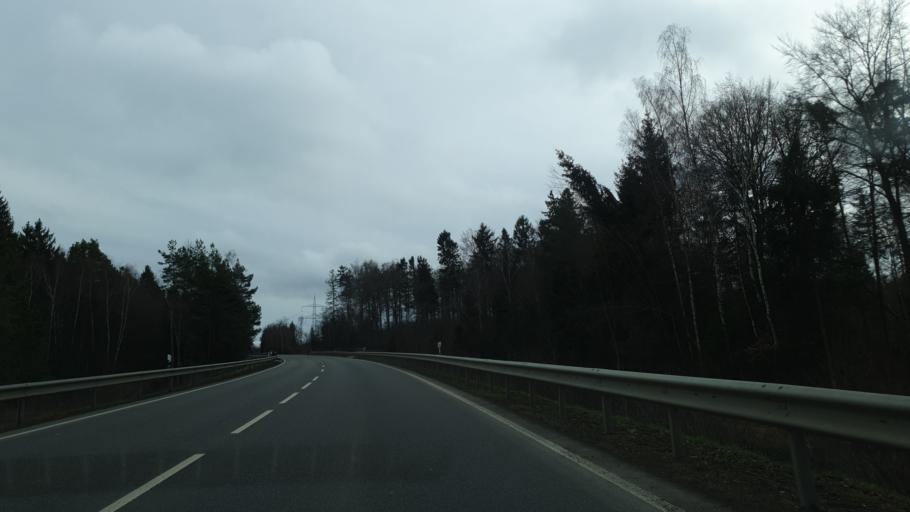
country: DE
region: Rheinland-Pfalz
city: Emmelshausen
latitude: 50.1641
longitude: 7.5695
